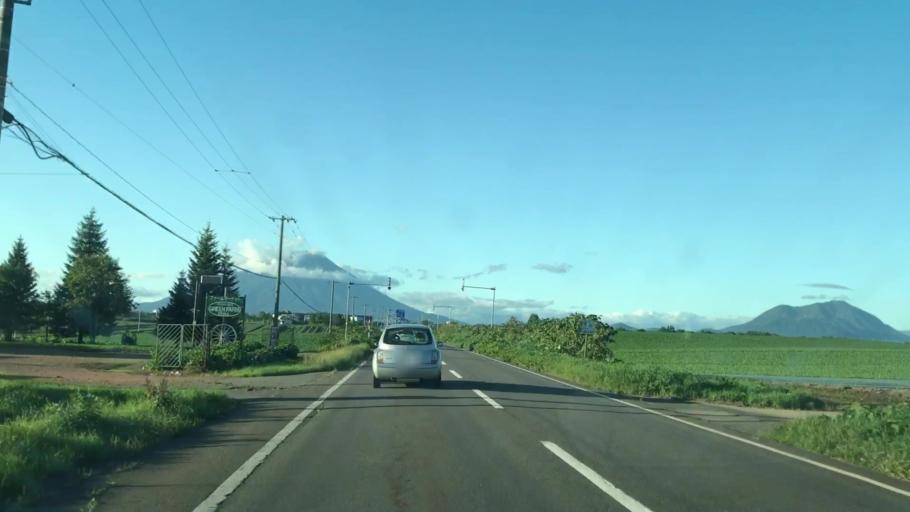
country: JP
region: Hokkaido
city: Niseko Town
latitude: 42.6569
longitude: 140.8113
